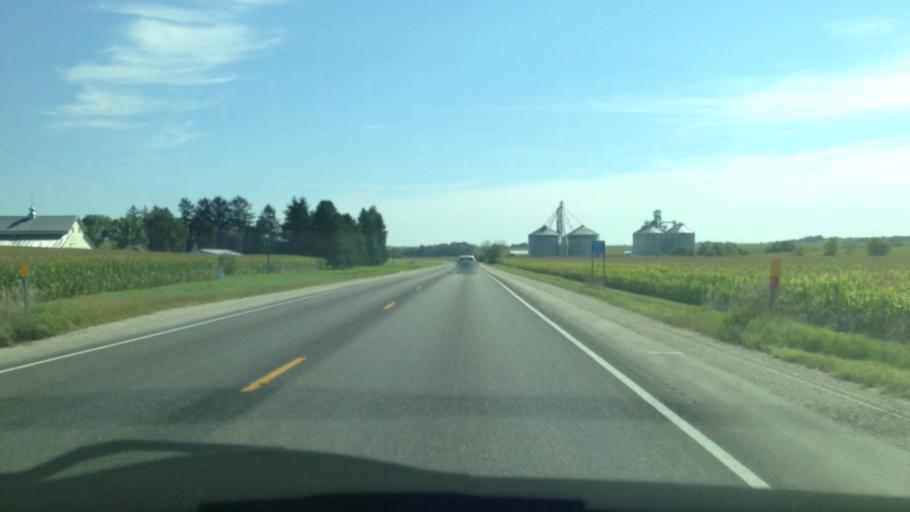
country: US
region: Minnesota
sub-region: Houston County
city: Spring Grove
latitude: 43.5149
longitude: -91.8014
